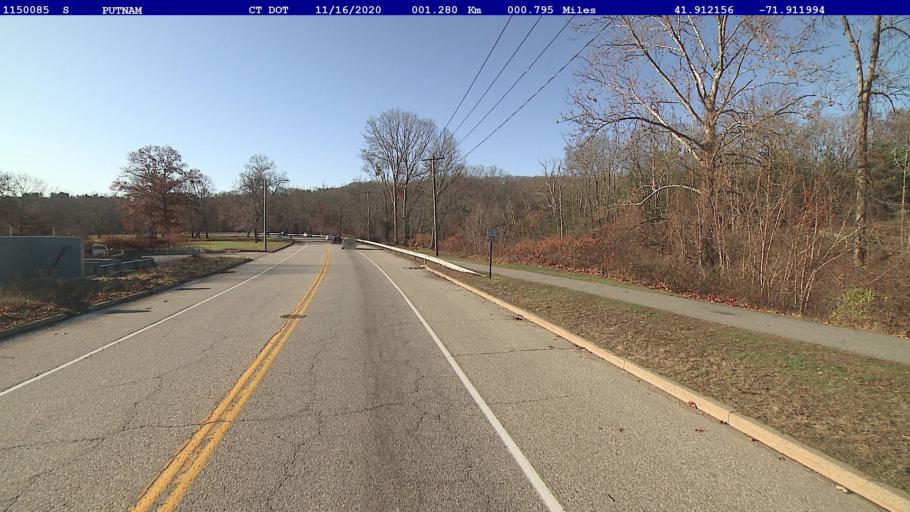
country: US
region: Connecticut
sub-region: Windham County
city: Putnam
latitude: 41.9121
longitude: -71.9120
